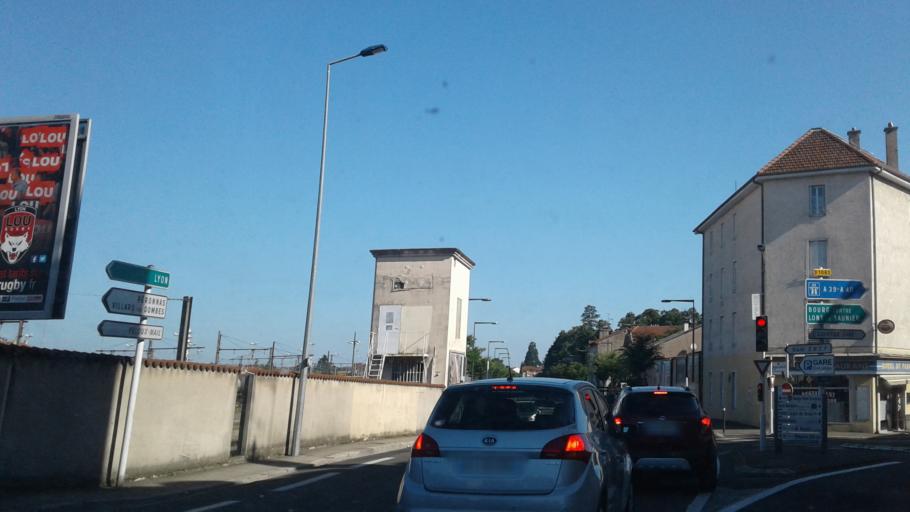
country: FR
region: Rhone-Alpes
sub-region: Departement de l'Ain
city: Peronnas
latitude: 46.1970
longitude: 5.2165
